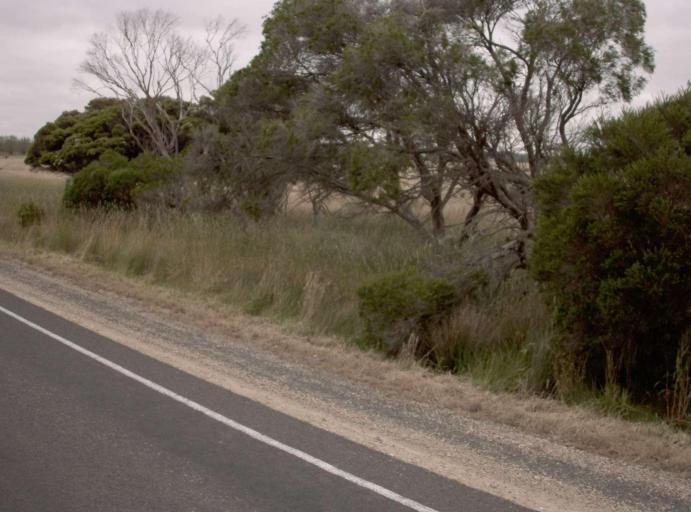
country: AU
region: Victoria
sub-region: Wellington
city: Sale
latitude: -38.0872
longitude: 146.9874
